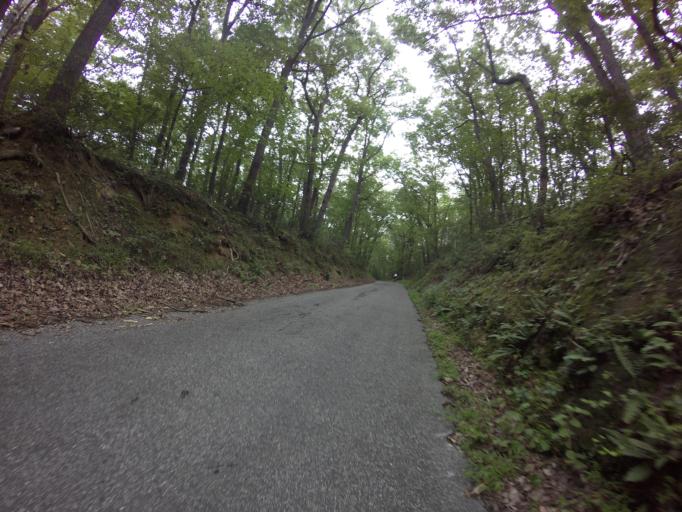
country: US
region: Maryland
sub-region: Baltimore County
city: Hunt Valley
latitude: 39.5555
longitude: -76.7084
